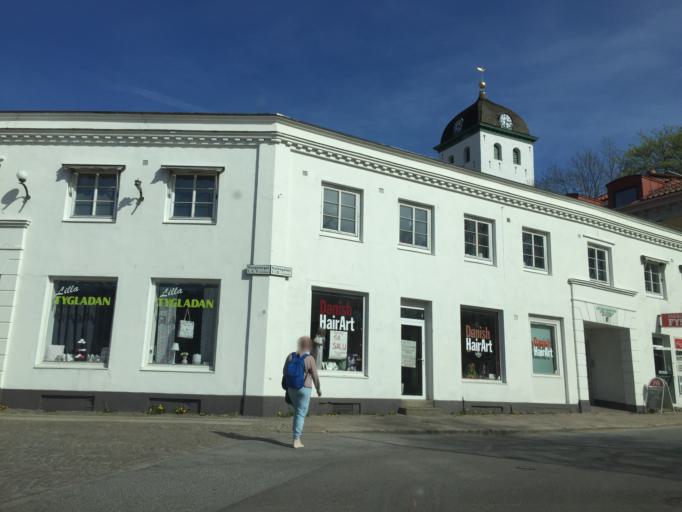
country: SE
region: Vaestra Goetaland
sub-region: Uddevalla Kommun
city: Uddevalla
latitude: 58.3487
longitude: 11.9385
